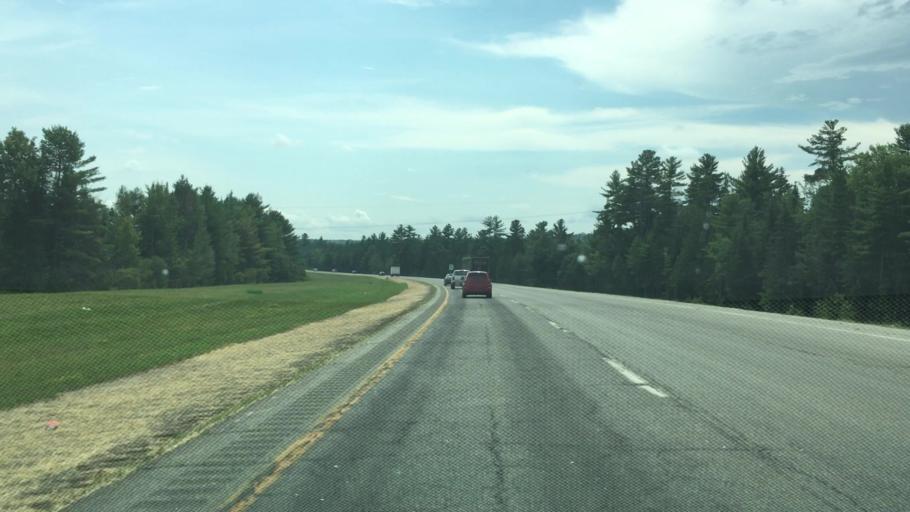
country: US
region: Maine
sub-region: Penobscot County
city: Medway
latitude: 45.5928
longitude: -68.5408
